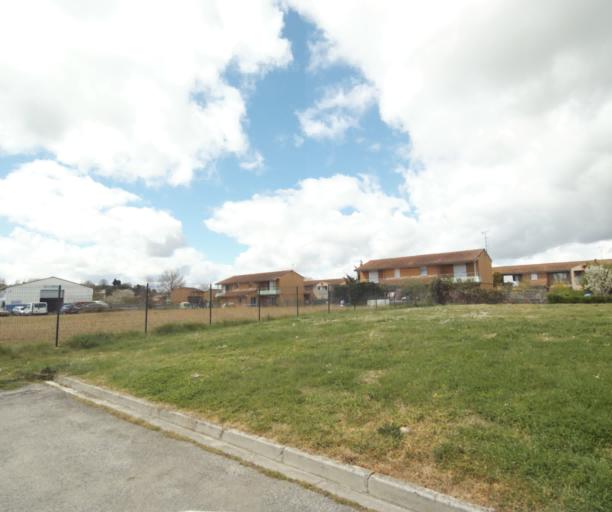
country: FR
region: Midi-Pyrenees
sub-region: Departement de l'Ariege
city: Saverdun
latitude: 43.2339
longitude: 1.5849
